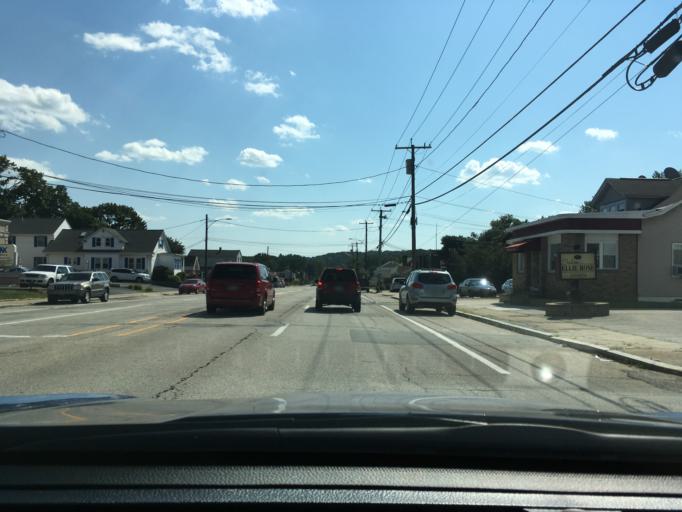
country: US
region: Rhode Island
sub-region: Providence County
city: Cranston
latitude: 41.7751
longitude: -71.4496
